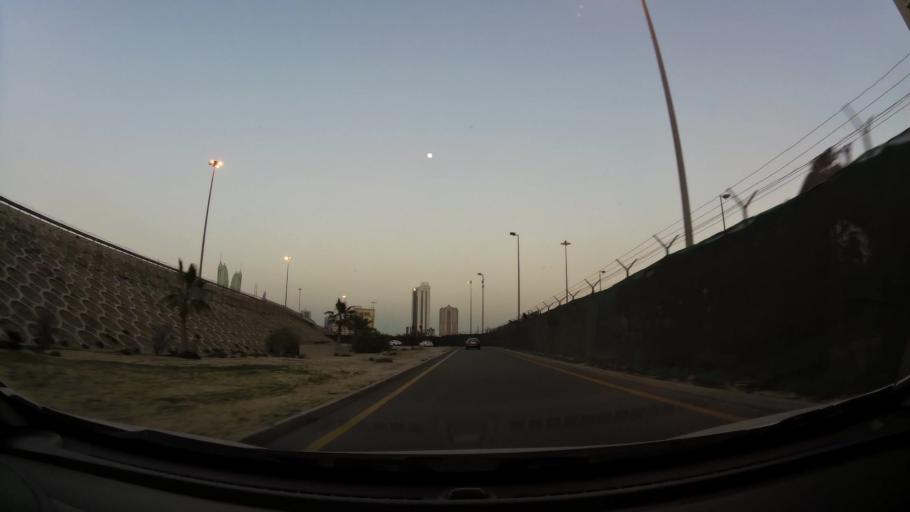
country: BH
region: Manama
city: Jidd Hafs
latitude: 26.2312
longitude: 50.5594
